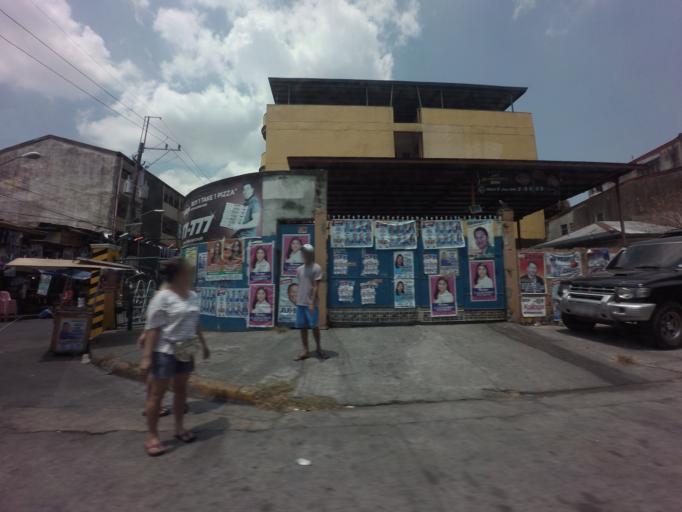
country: PH
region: Metro Manila
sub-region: Mandaluyong
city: Mandaluyong City
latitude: 14.5728
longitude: 121.0256
